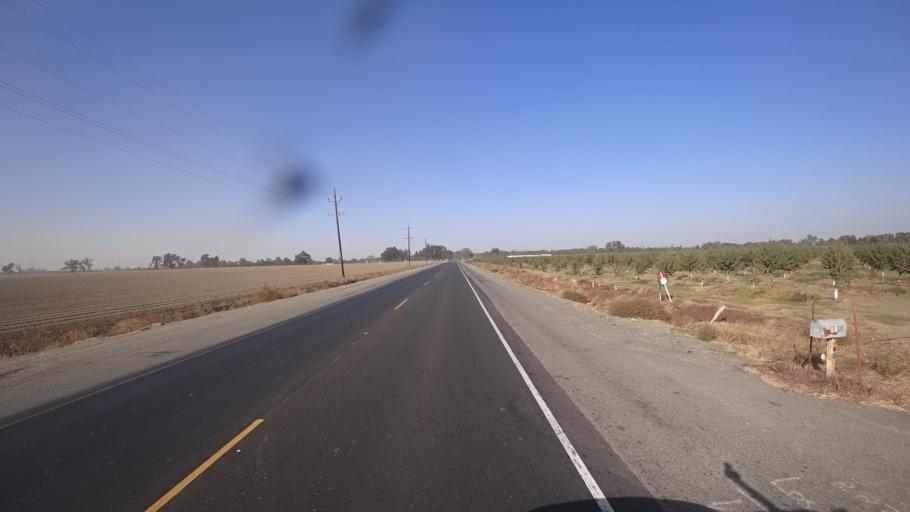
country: US
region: California
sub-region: Yolo County
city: Woodland
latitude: 38.7852
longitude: -121.7284
